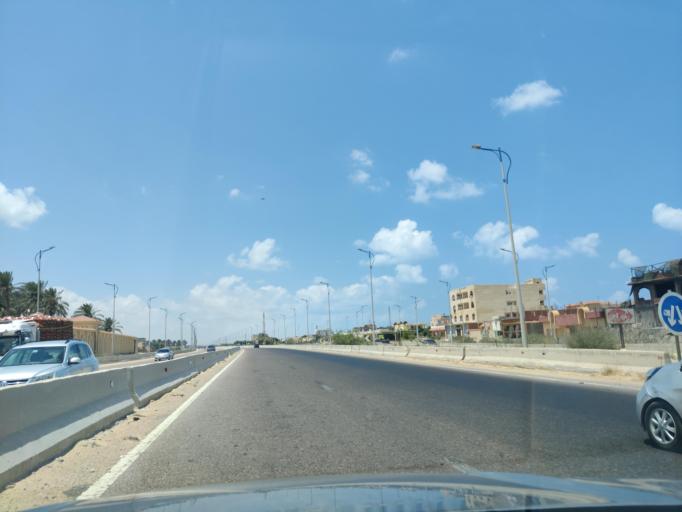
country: EG
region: Alexandria
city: Alexandria
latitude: 30.9862
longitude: 29.5868
